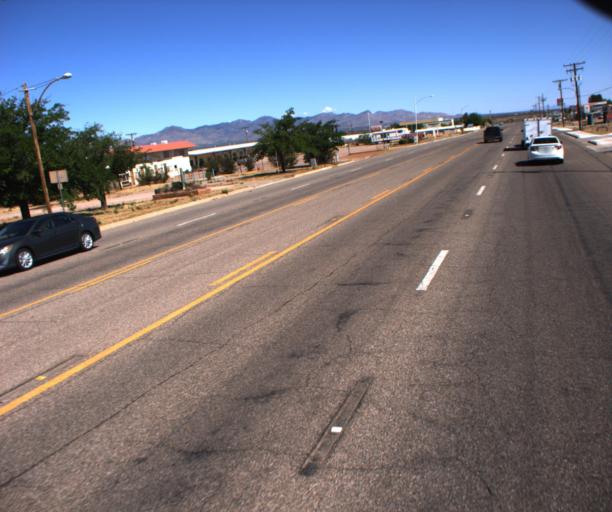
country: US
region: Arizona
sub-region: Cochise County
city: Huachuca City
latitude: 31.6251
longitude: -110.3355
